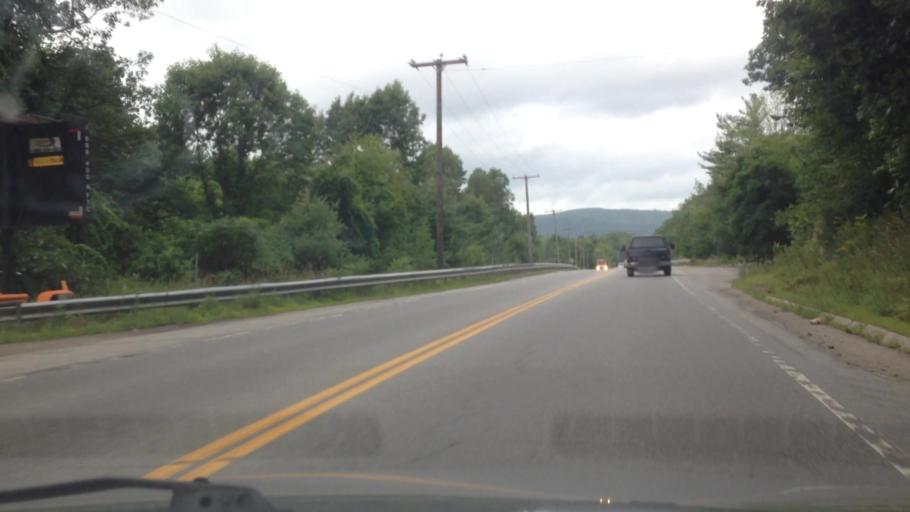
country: US
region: New Hampshire
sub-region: Cheshire County
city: Keene
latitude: 42.9149
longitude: -72.2536
